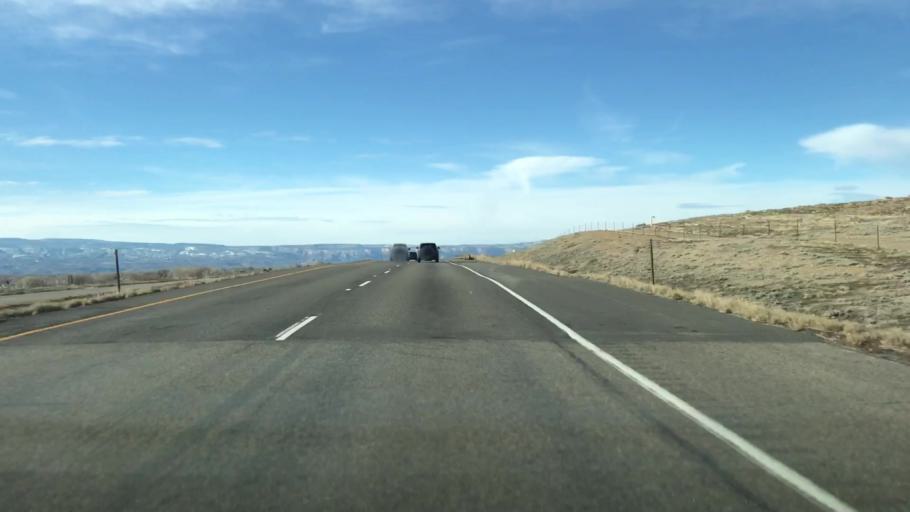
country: US
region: Colorado
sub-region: Mesa County
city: Clifton
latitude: 39.1134
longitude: -108.4074
